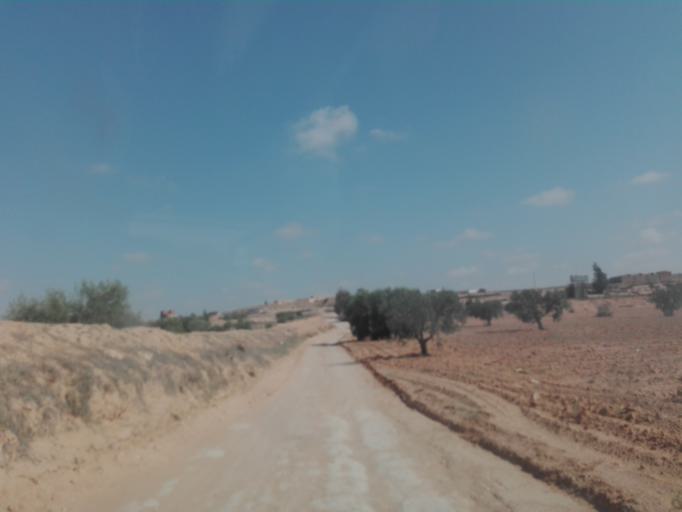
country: TN
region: Madanin
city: Medenine
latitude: 33.4372
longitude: 10.4314
